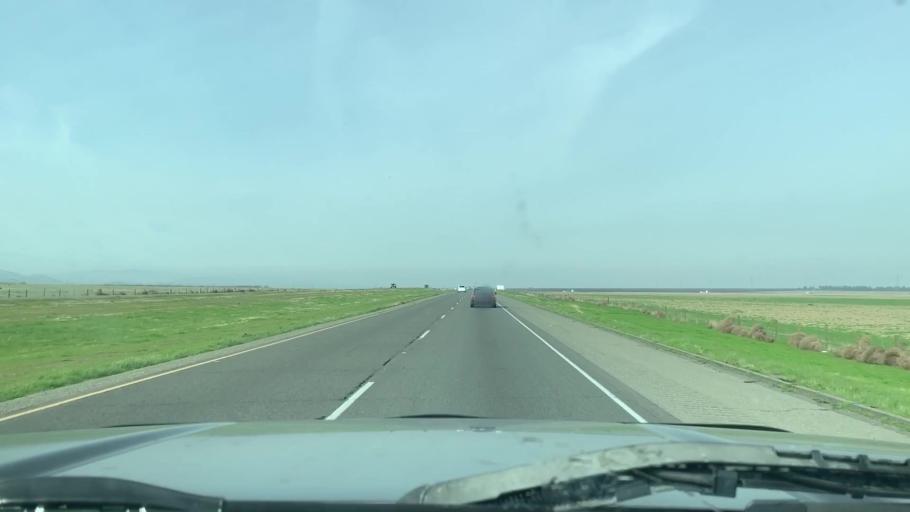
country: US
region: California
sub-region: Fresno County
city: Coalinga
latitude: 36.3439
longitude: -120.3118
